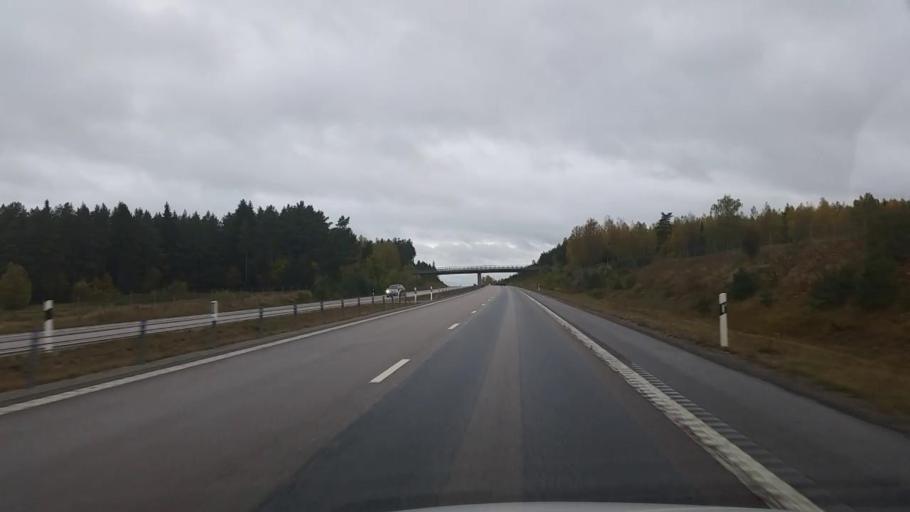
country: SE
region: Uppsala
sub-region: Osthammars Kommun
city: Bjorklinge
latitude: 60.1293
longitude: 17.5473
